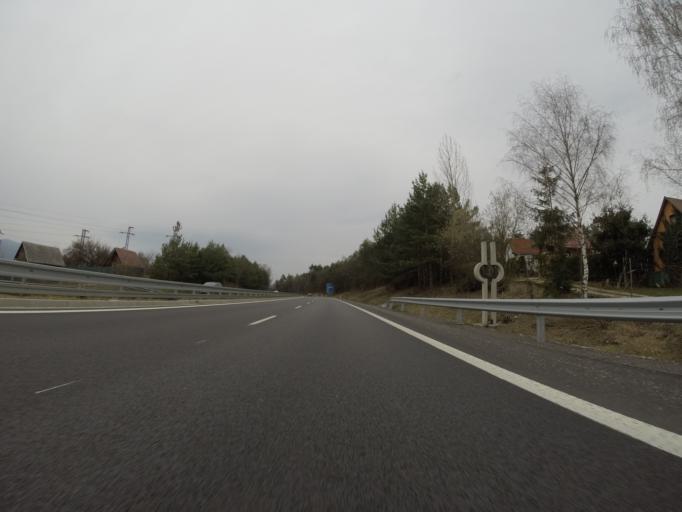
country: SK
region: Nitriansky
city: Prievidza
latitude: 48.7495
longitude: 18.6263
